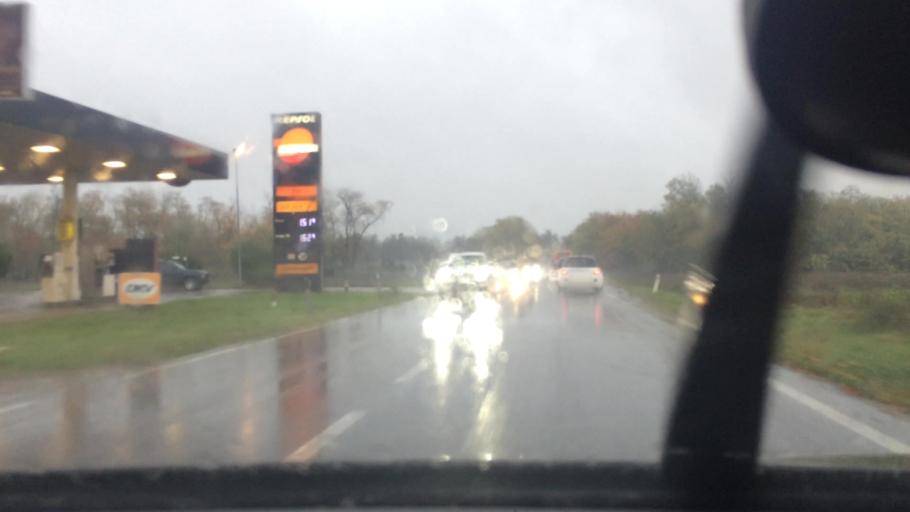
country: IT
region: Lombardy
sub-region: Citta metropolitana di Milano
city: Casorezzo
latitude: 45.5458
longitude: 8.9096
